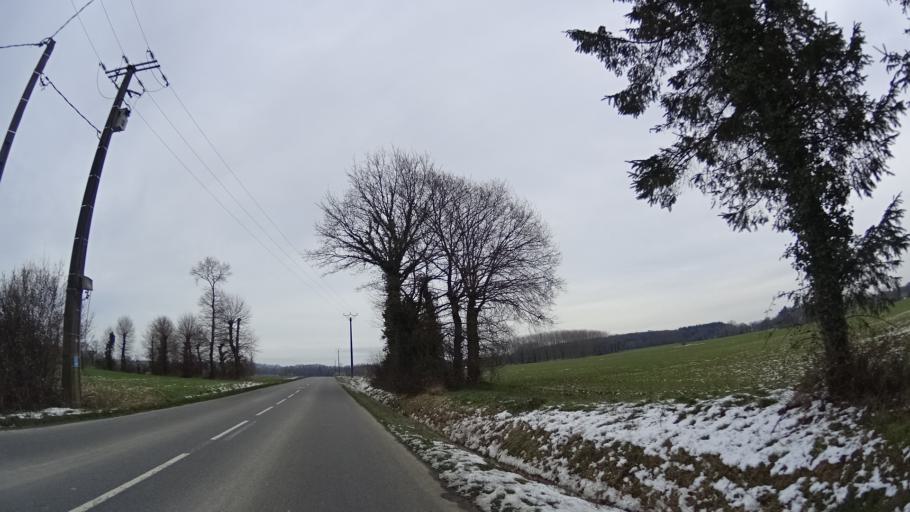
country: FR
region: Brittany
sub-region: Departement d'Ille-et-Vilaine
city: Irodouer
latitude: 48.2618
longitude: -1.9855
